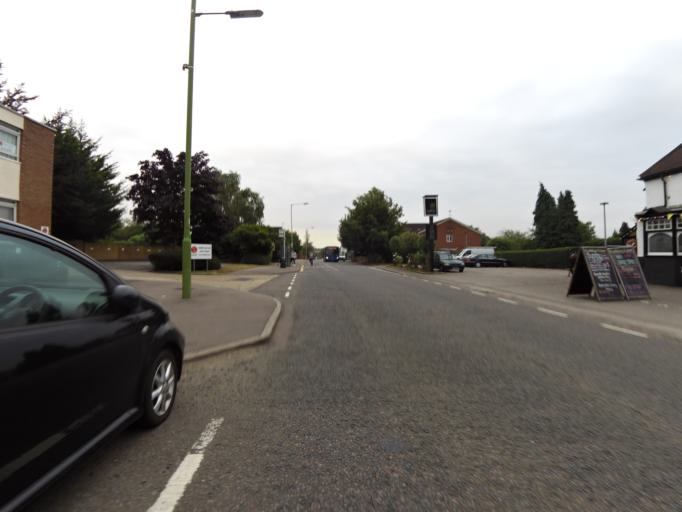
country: GB
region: England
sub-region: Hertfordshire
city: Shenley AV
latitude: 51.7221
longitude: -0.2938
